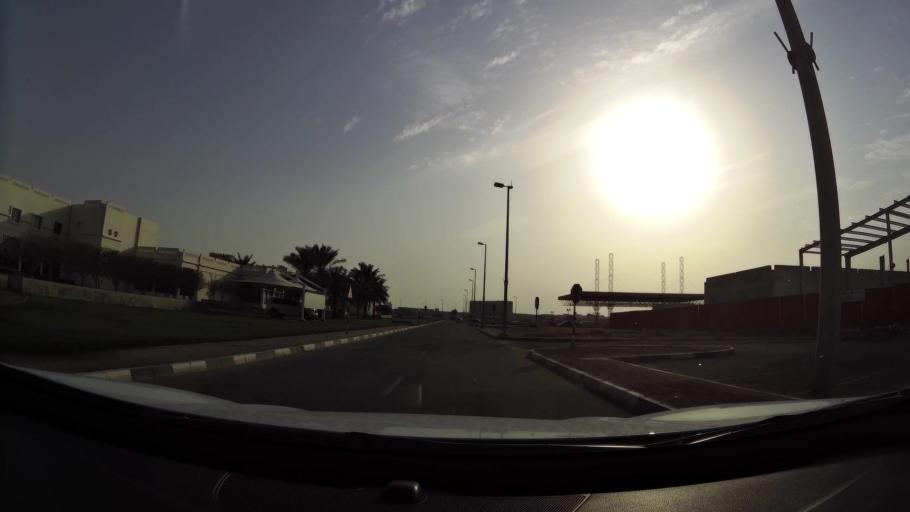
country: AE
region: Abu Dhabi
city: Abu Dhabi
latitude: 24.3295
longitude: 54.5195
